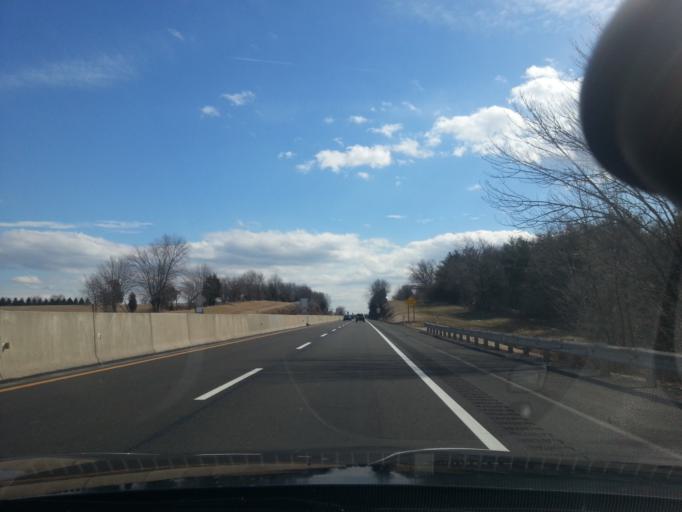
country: US
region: Pennsylvania
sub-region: Montgomery County
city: Harleysville
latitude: 40.3072
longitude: -75.3726
